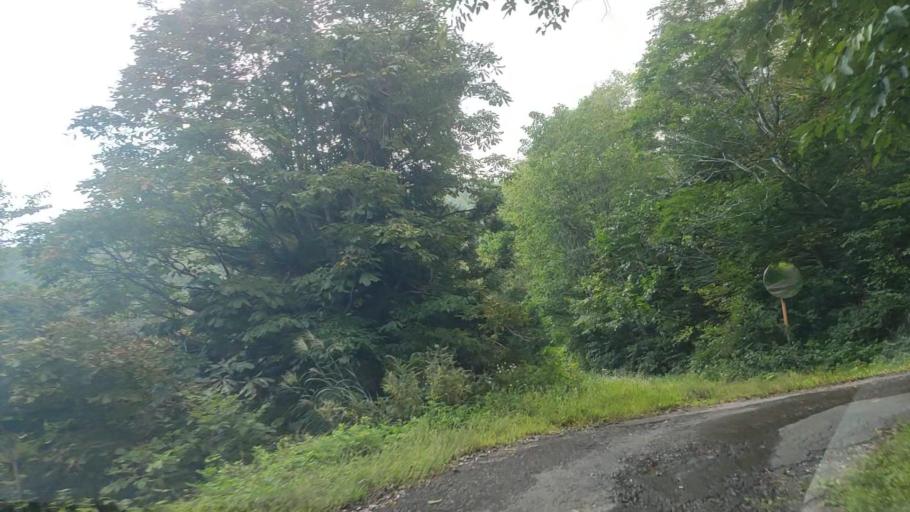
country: JP
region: Toyama
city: Yatsuomachi-higashikumisaka
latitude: 36.3322
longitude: 137.0753
